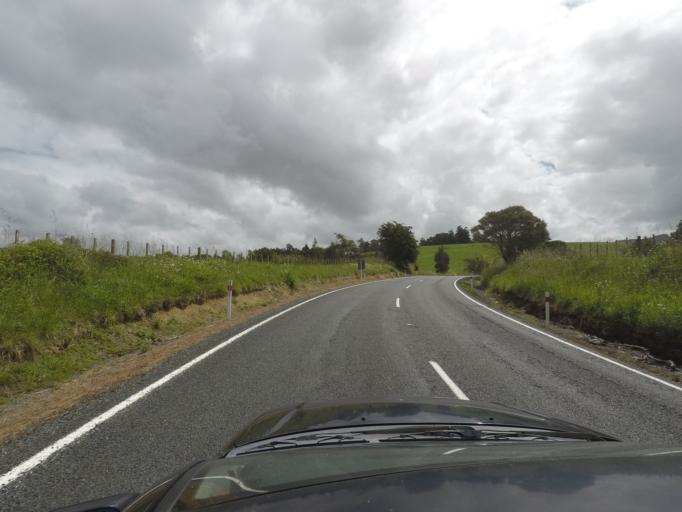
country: NZ
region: Auckland
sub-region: Auckland
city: Parakai
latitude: -36.5044
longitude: 174.5080
